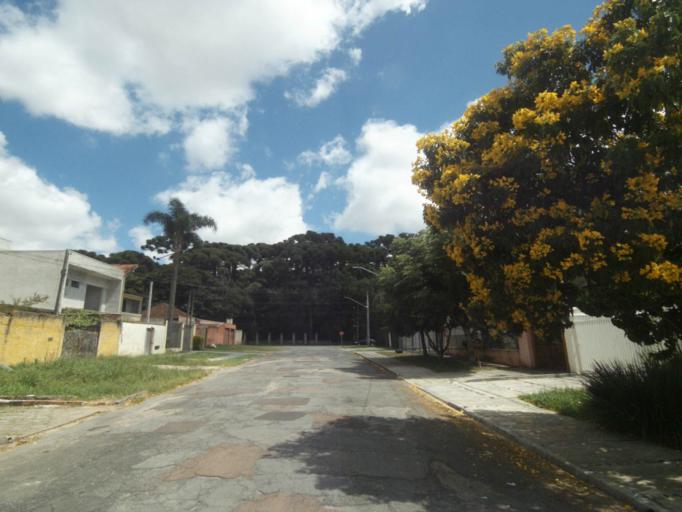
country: BR
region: Parana
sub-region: Pinhais
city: Pinhais
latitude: -25.4367
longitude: -49.2180
